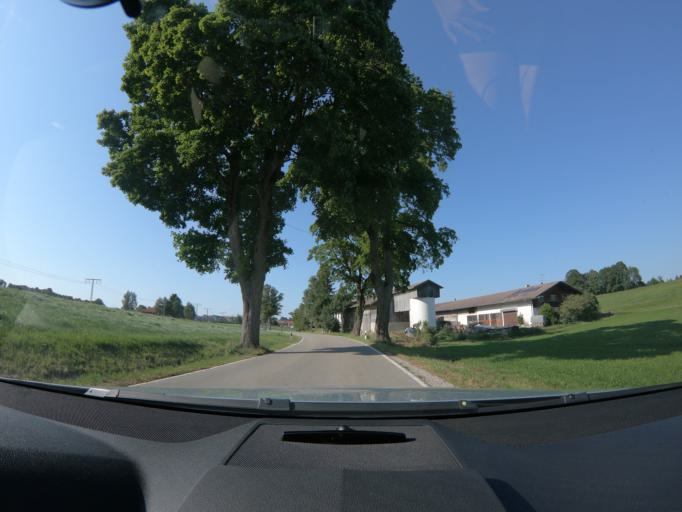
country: DE
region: Bavaria
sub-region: Upper Bavaria
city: Holzkirchen
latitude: 47.8702
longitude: 11.7090
